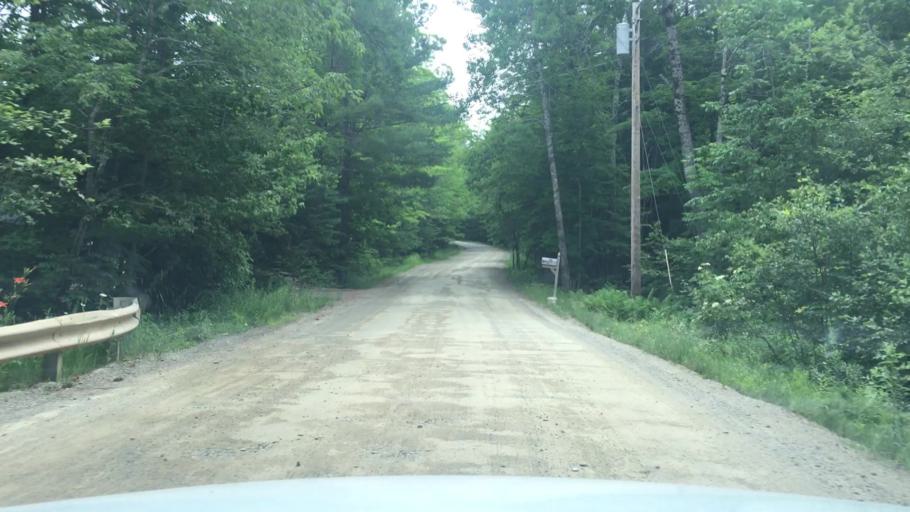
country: US
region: Maine
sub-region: Kennebec County
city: Albion
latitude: 44.4550
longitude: -69.3222
